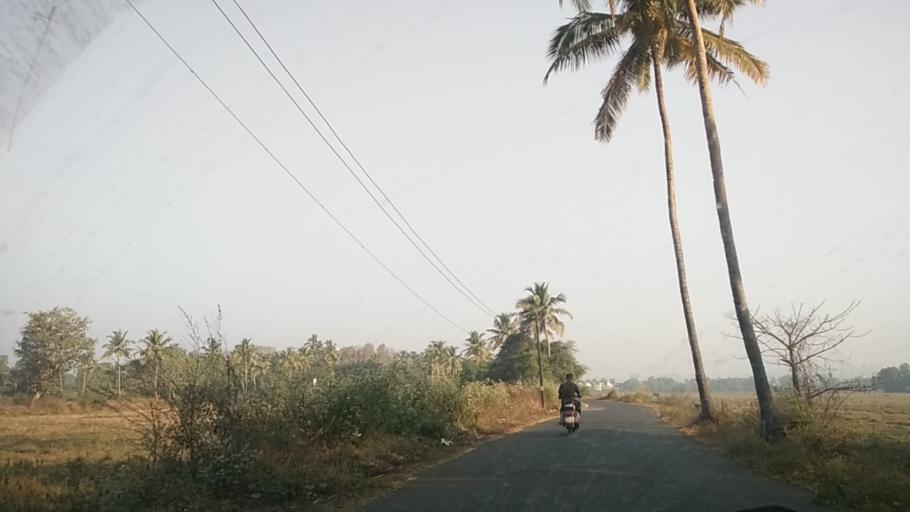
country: IN
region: Goa
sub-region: South Goa
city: Benaulim
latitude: 15.2712
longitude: 73.9381
